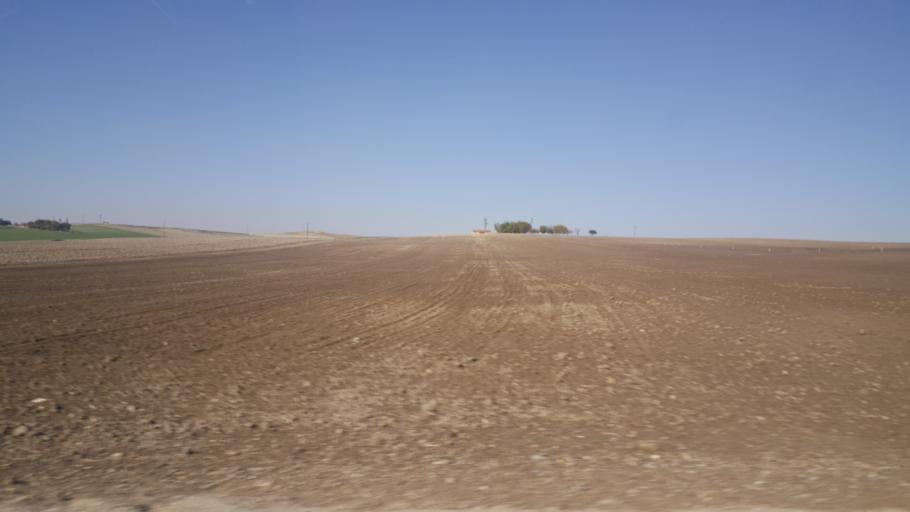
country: TR
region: Konya
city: Celtik
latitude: 39.0667
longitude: 31.8990
